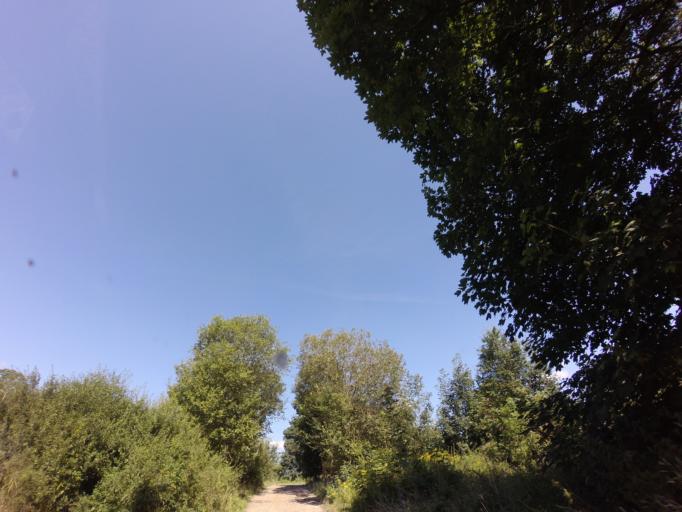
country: PL
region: West Pomeranian Voivodeship
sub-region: Powiat choszczenski
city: Recz
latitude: 53.1679
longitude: 15.5773
